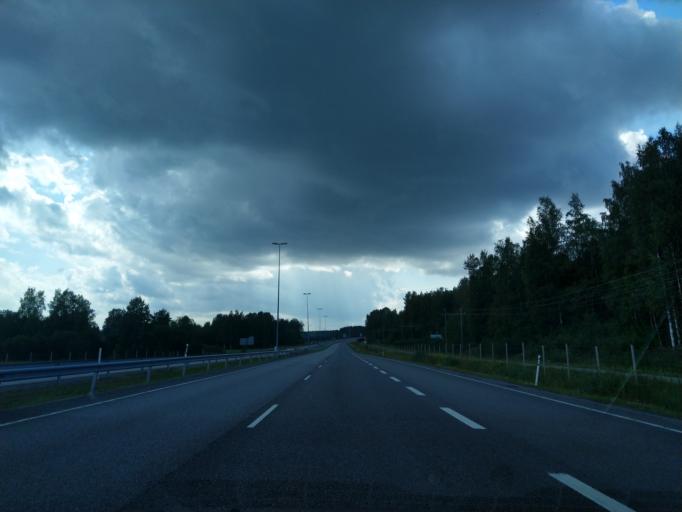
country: FI
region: South Karelia
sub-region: Imatra
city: Imatra
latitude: 61.1702
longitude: 28.6928
